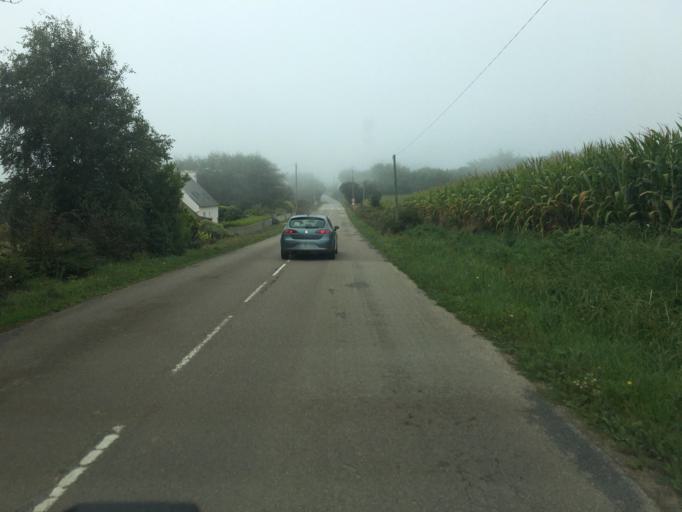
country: FR
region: Brittany
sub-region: Departement du Finistere
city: Plogoff
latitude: 48.0635
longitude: -4.6161
